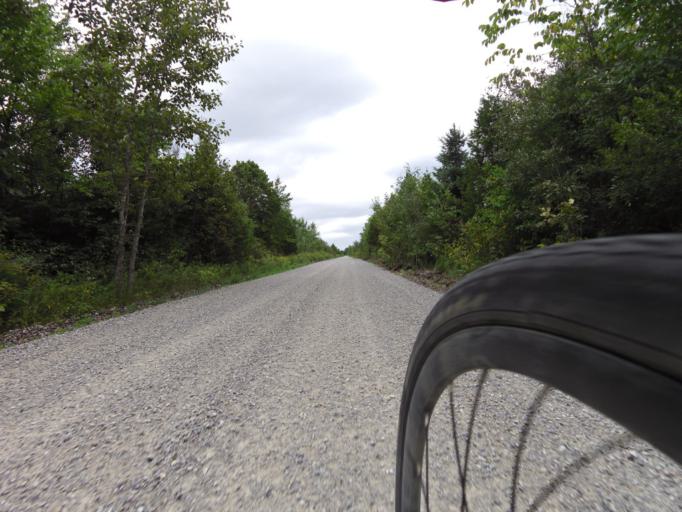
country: CA
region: Ontario
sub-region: Lanark County
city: Smiths Falls
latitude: 44.9470
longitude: -76.0424
